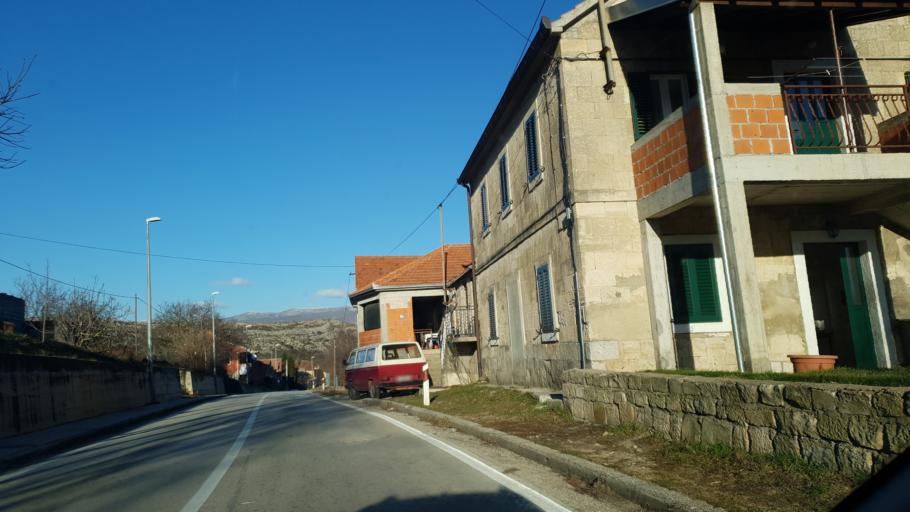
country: HR
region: Splitsko-Dalmatinska
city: Sinj
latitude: 43.7123
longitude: 16.6604
